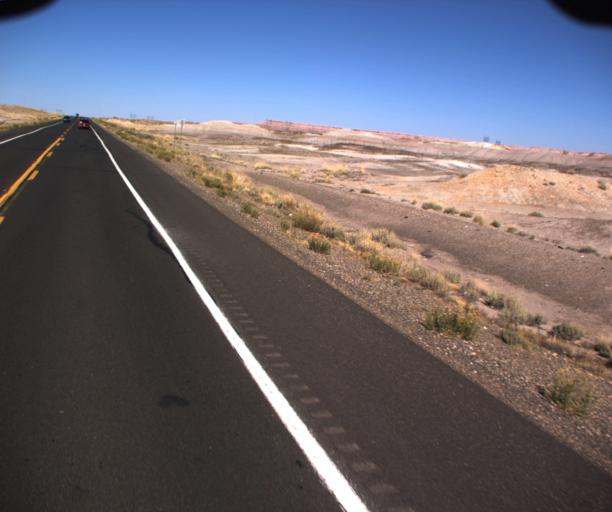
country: US
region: Arizona
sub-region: Coconino County
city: Tuba City
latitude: 35.9596
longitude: -111.3973
